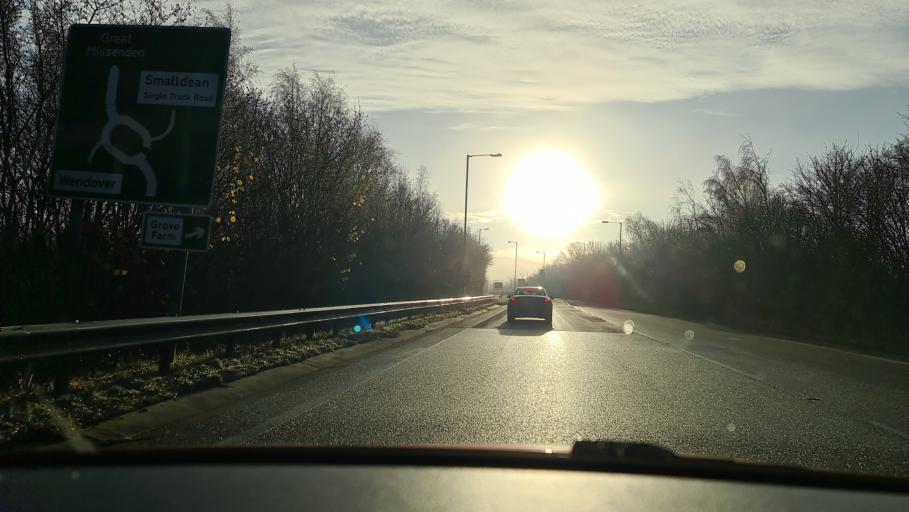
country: GB
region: England
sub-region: Buckinghamshire
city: Wendover
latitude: 51.7543
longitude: -0.7388
